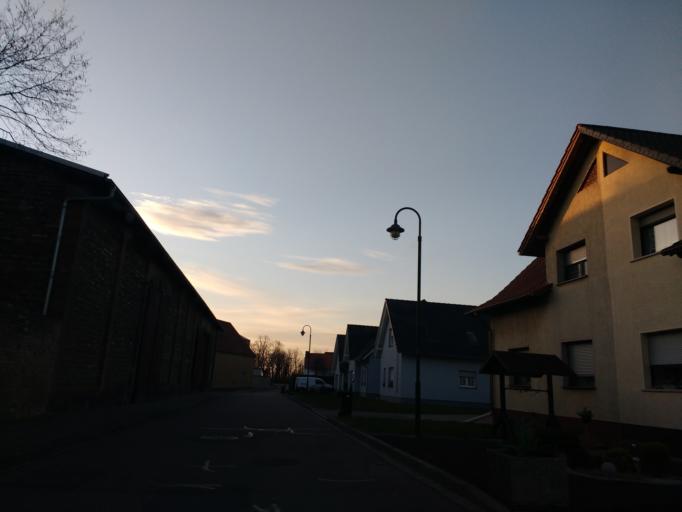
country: DE
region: Saxony-Anhalt
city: Loberitz
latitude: 51.6219
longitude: 12.1736
